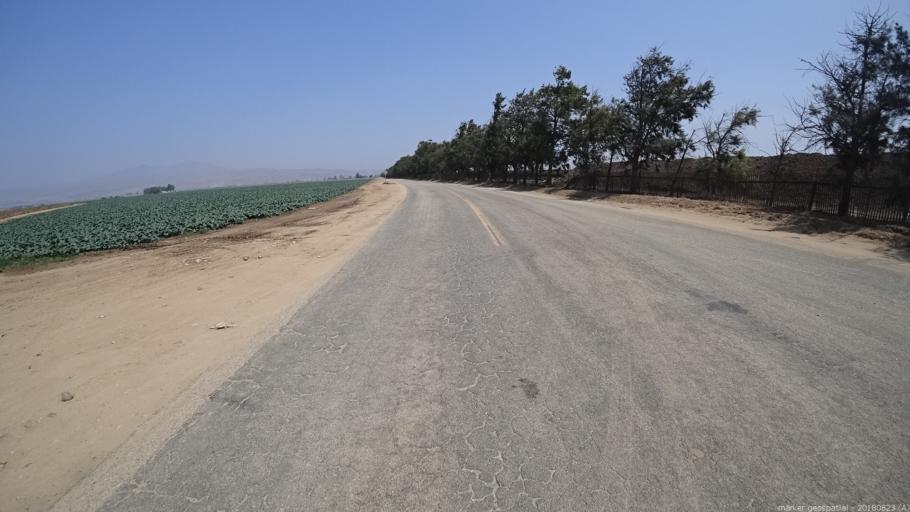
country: US
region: California
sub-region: Monterey County
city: Greenfield
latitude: 36.3290
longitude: -121.2789
